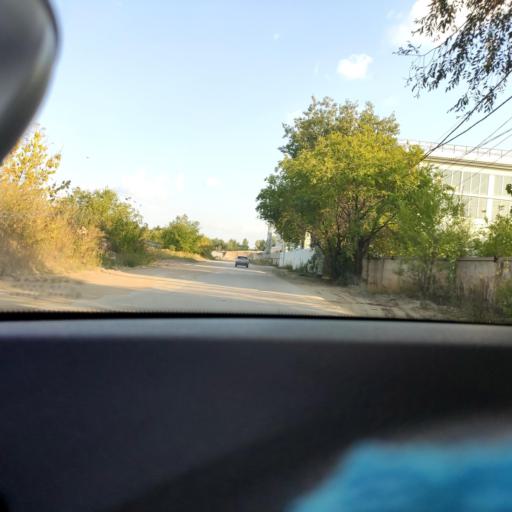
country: RU
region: Samara
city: Samara
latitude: 53.1808
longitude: 50.2652
